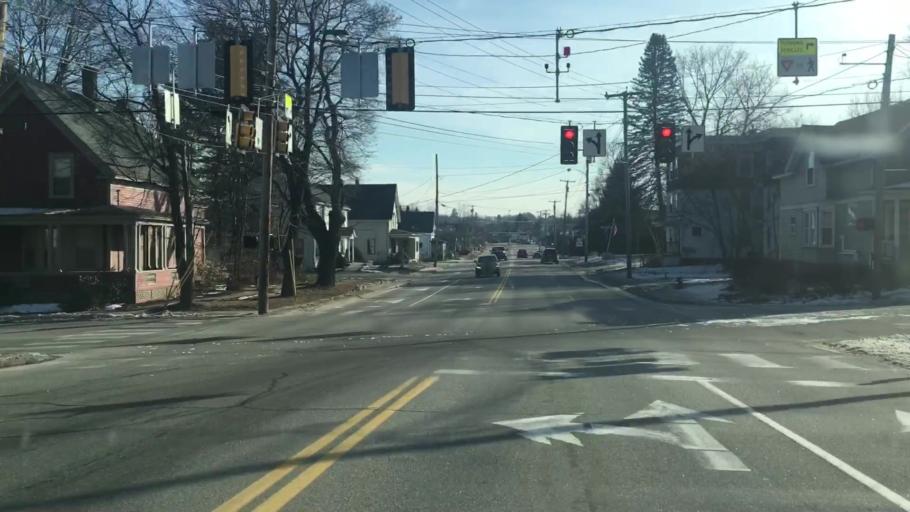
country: US
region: Maine
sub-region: Androscoggin County
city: Lewiston
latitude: 44.1034
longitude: -70.1922
